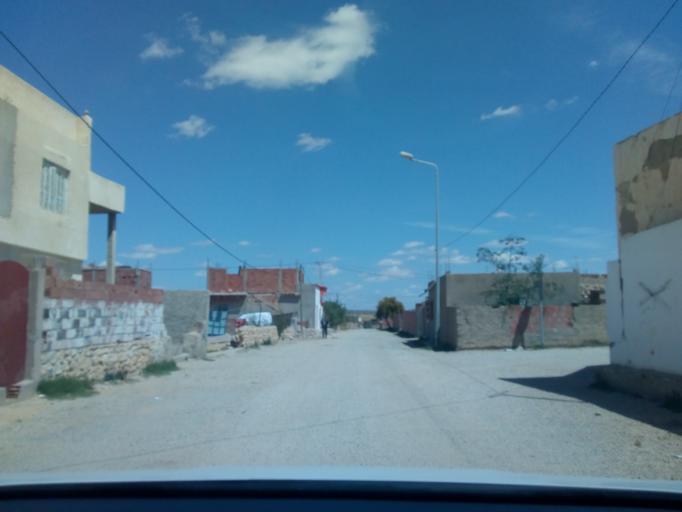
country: TN
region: Safaqis
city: Sfax
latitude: 34.7295
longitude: 10.4916
